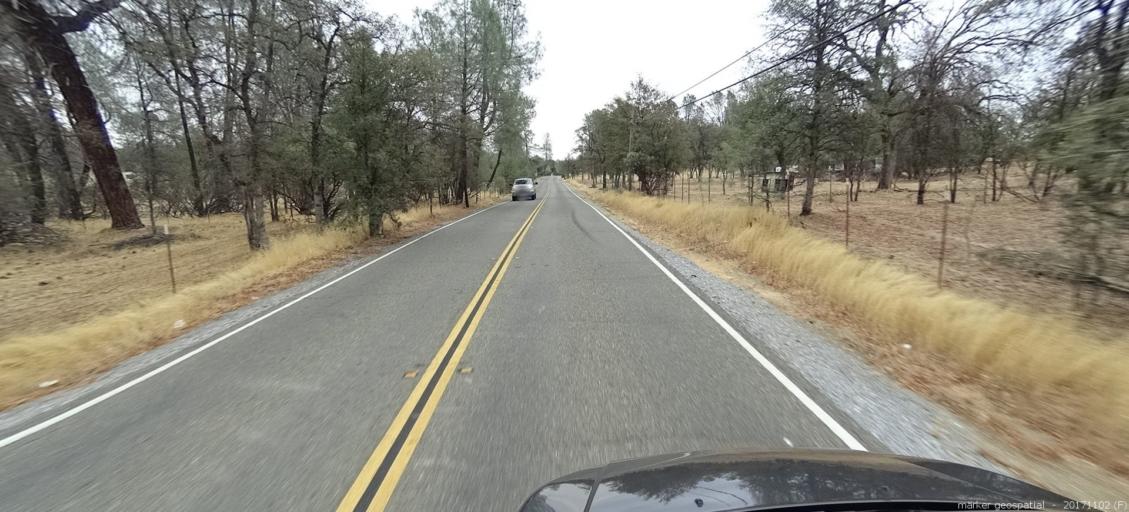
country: US
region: California
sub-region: Shasta County
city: Shasta Lake
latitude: 40.6715
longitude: -122.3176
